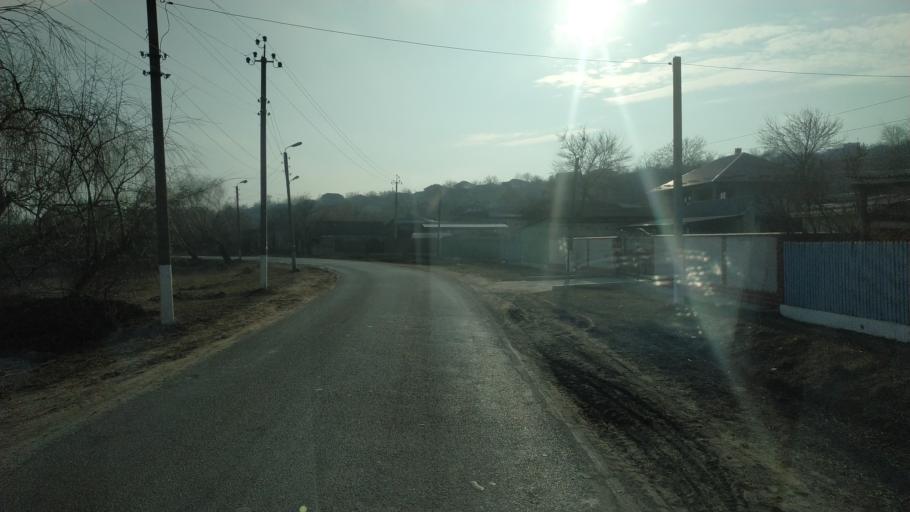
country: MD
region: Hincesti
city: Dancu
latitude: 46.7759
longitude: 28.3466
